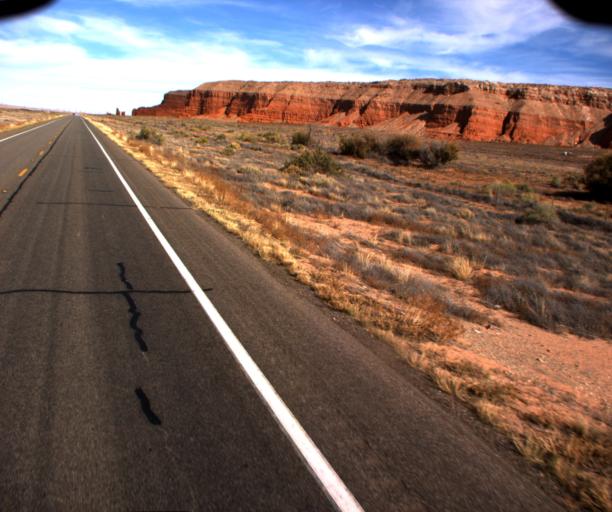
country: US
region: Arizona
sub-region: Navajo County
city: Kayenta
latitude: 36.7677
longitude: -110.0308
